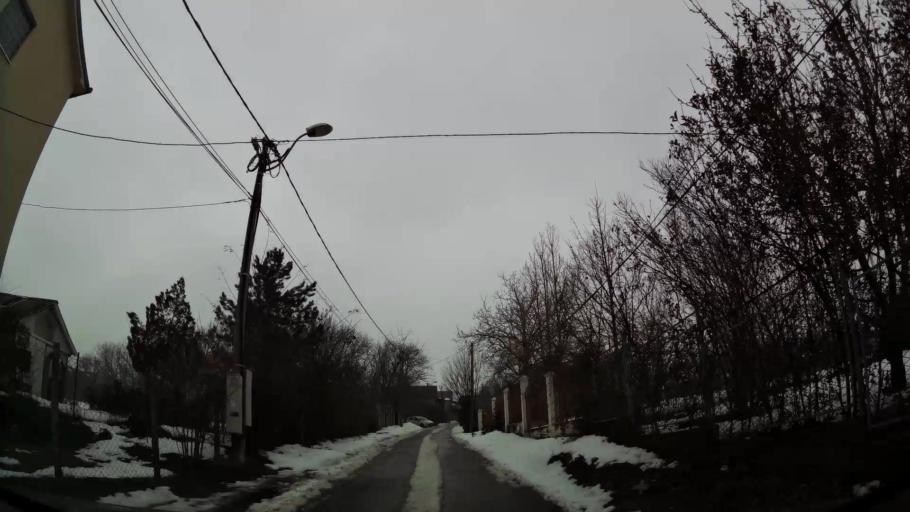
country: RS
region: Central Serbia
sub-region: Belgrade
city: Zvezdara
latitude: 44.7628
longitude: 20.5157
